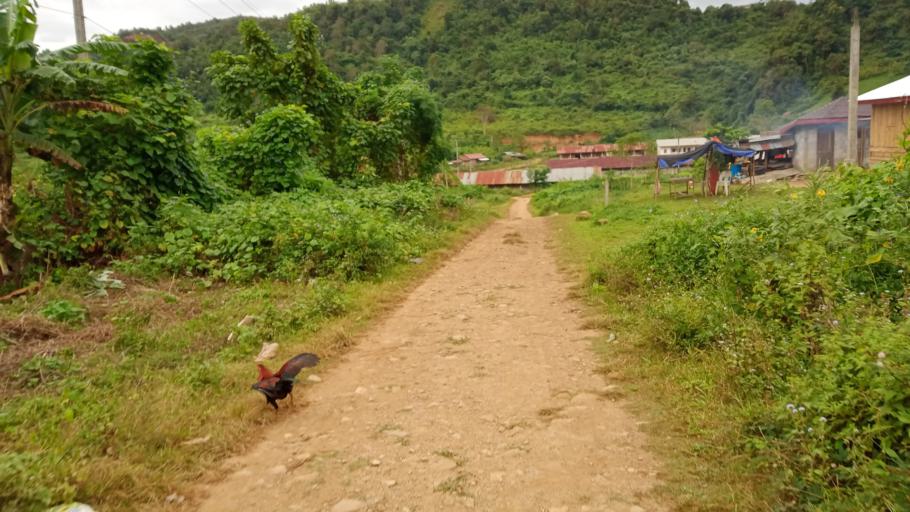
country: LA
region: Xiangkhoang
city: Phonsavan
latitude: 19.1147
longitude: 102.9141
